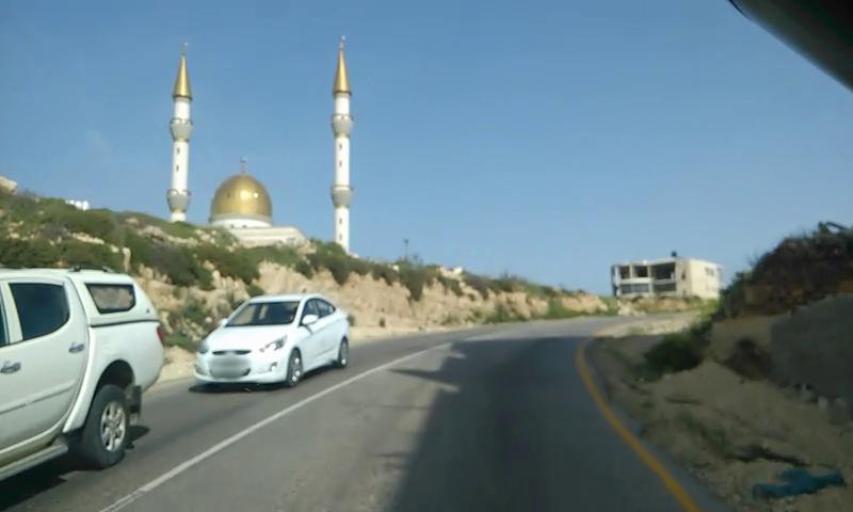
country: PS
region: West Bank
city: Surda
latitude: 31.9356
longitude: 35.2072
